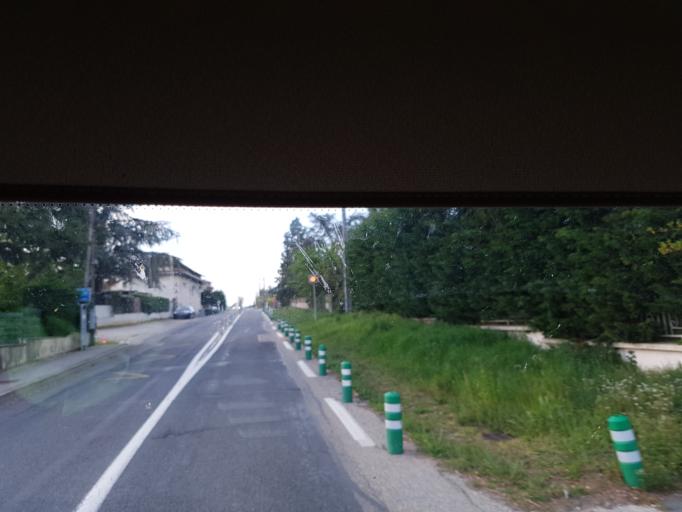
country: FR
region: Rhone-Alpes
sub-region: Departement du Rhone
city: Sainte-Consorce
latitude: 45.7938
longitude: 4.6894
